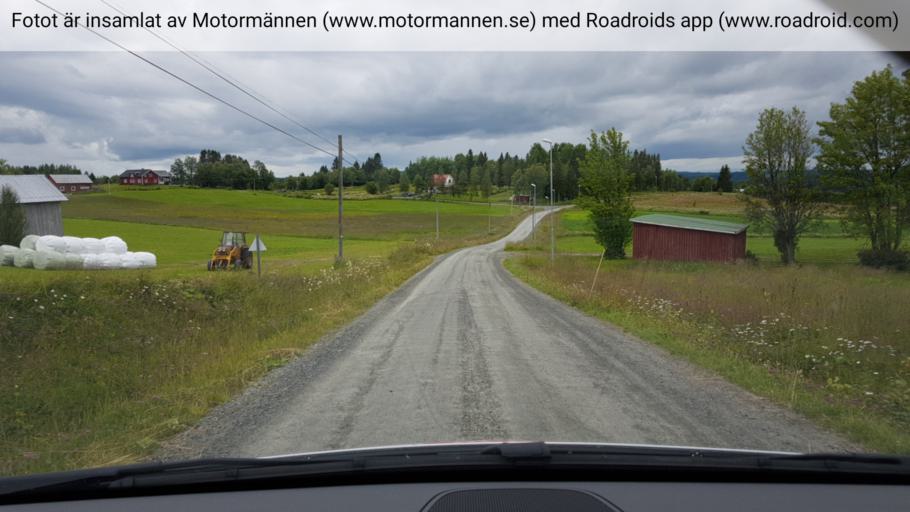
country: SE
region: Jaemtland
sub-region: Krokoms Kommun
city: Valla
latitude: 63.5209
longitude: 13.8905
